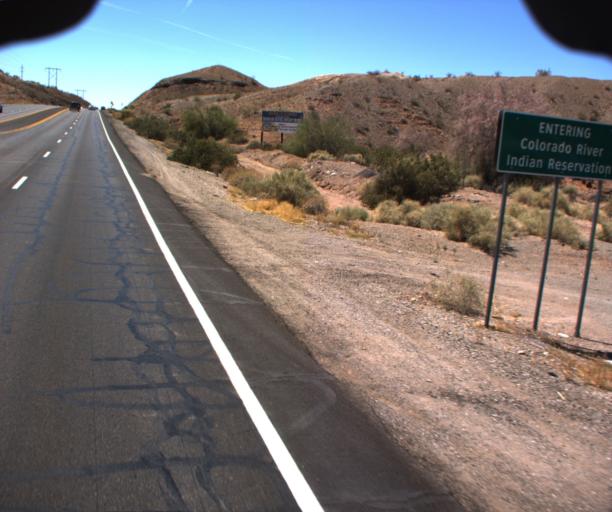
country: US
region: Arizona
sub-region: La Paz County
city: Cienega Springs
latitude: 34.1827
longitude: -114.2274
